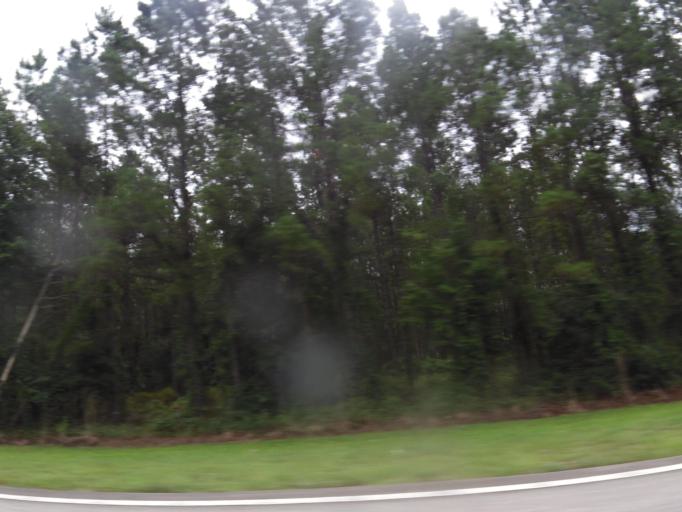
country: US
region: Florida
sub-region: Saint Johns County
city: Saint Augustine South
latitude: 29.8560
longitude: -81.4532
